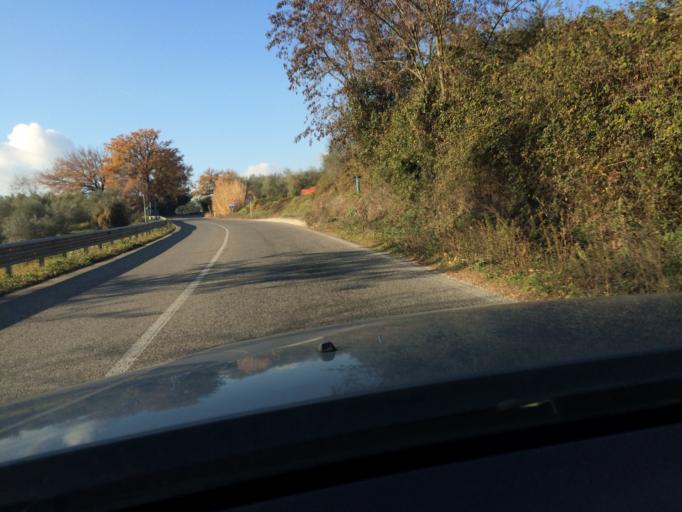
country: IT
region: Umbria
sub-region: Provincia di Terni
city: Fornole
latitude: 42.5518
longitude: 12.4436
